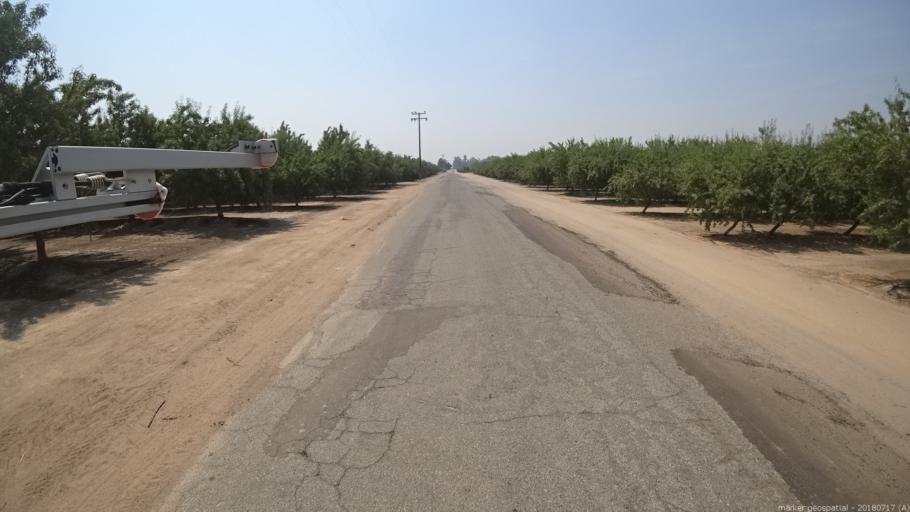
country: US
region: California
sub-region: Madera County
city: Fairmead
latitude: 37.1359
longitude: -120.1382
